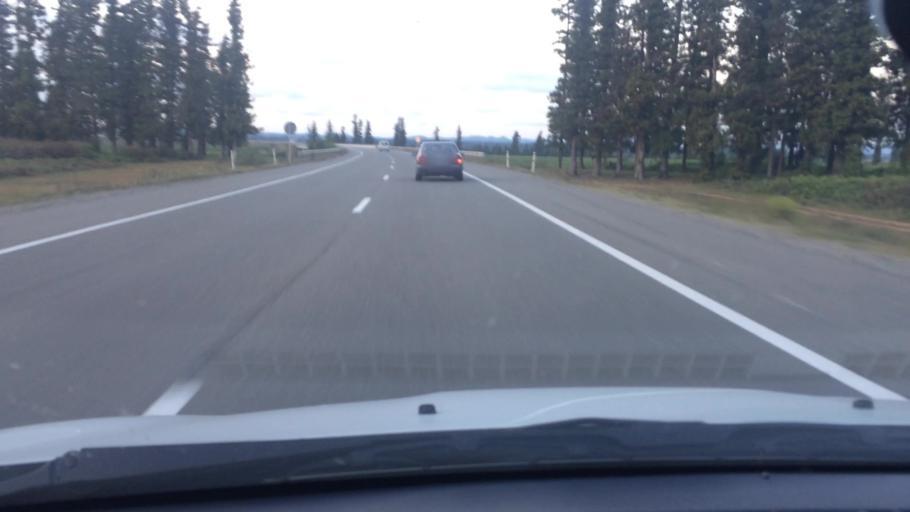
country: GE
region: Ajaria
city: Ochkhamuri
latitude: 41.8566
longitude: 41.8383
